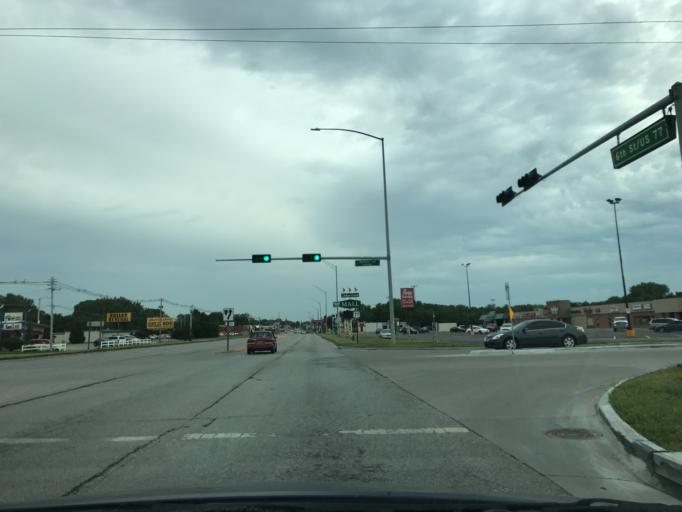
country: US
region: Nebraska
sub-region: Gage County
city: Beatrice
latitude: 40.2892
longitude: -96.7466
